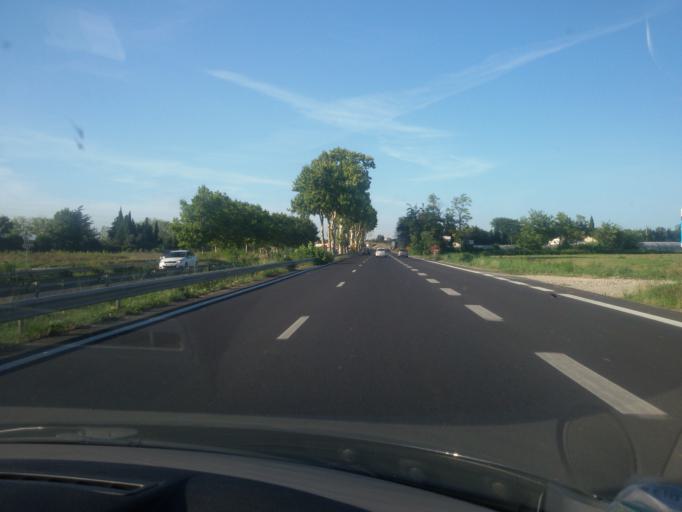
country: FR
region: Languedoc-Roussillon
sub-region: Departement de l'Herault
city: Lattes
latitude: 43.5757
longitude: 3.8972
